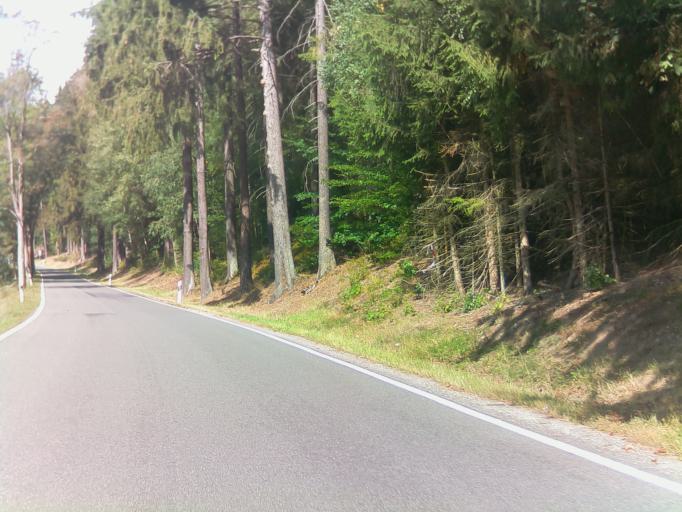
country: DE
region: Thuringia
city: Schwarza
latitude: 50.6325
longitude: 10.5314
